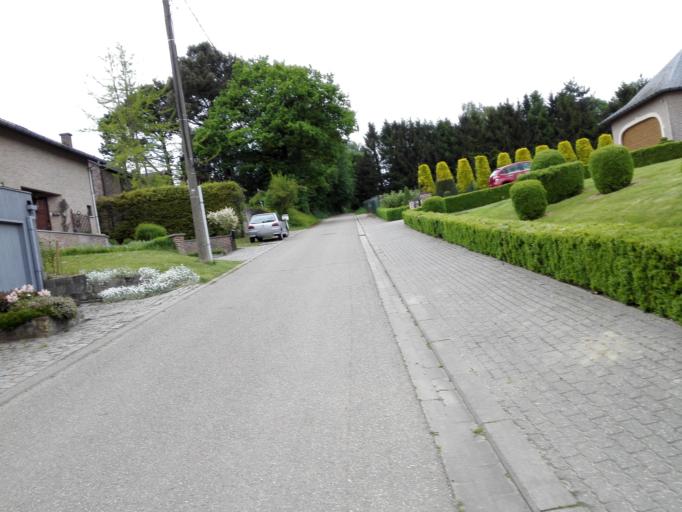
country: BE
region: Flanders
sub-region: Provincie Vlaams-Brabant
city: Huldenberg
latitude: 50.7914
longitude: 4.5792
